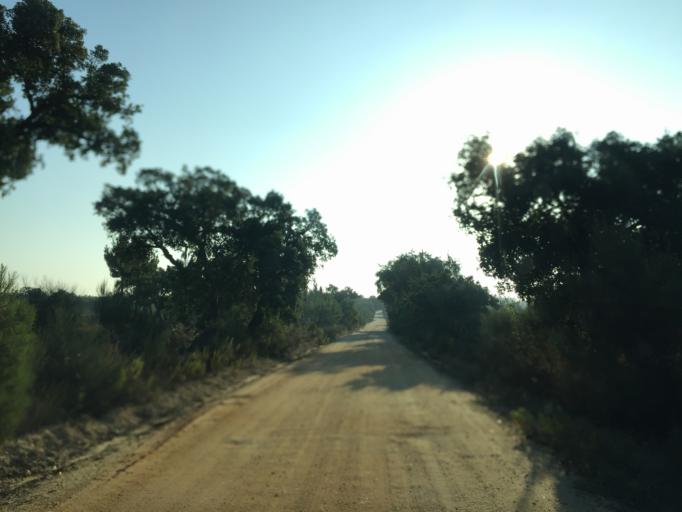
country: PT
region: Portalegre
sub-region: Ponte de Sor
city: Santo Andre
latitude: 39.1644
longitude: -8.2886
